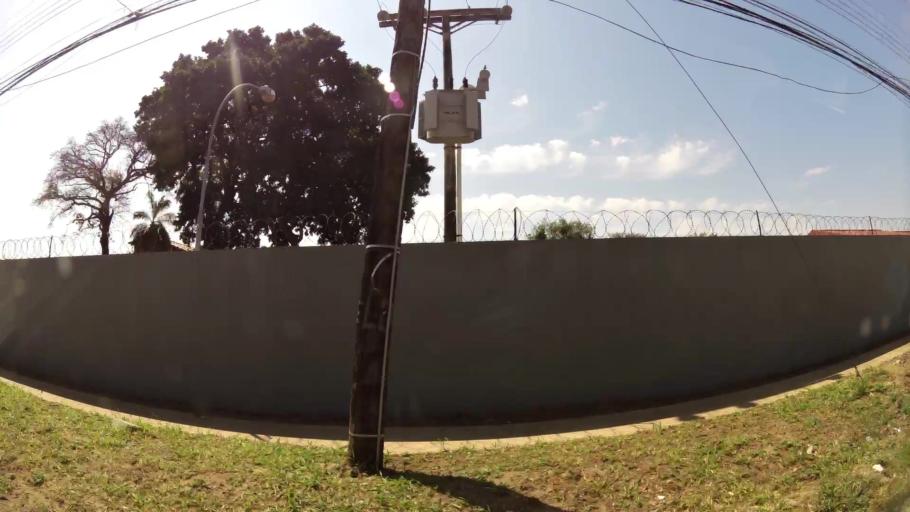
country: BO
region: Santa Cruz
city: Santa Cruz de la Sierra
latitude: -17.7439
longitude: -63.1579
